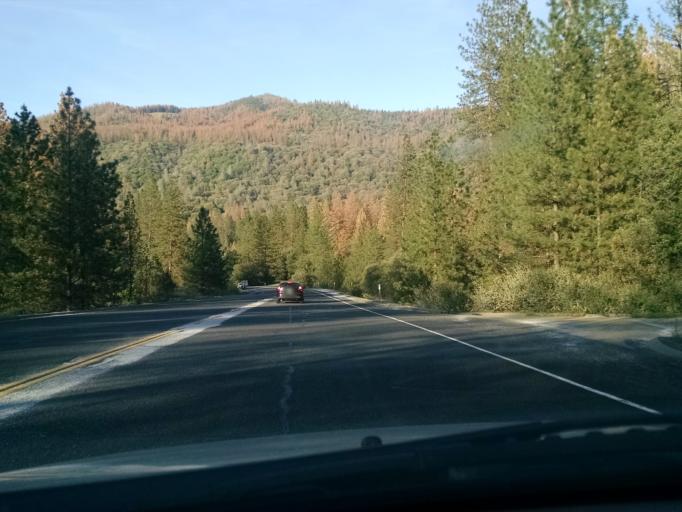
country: US
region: California
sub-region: Madera County
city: Ahwahnee
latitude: 37.4191
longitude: -119.7283
